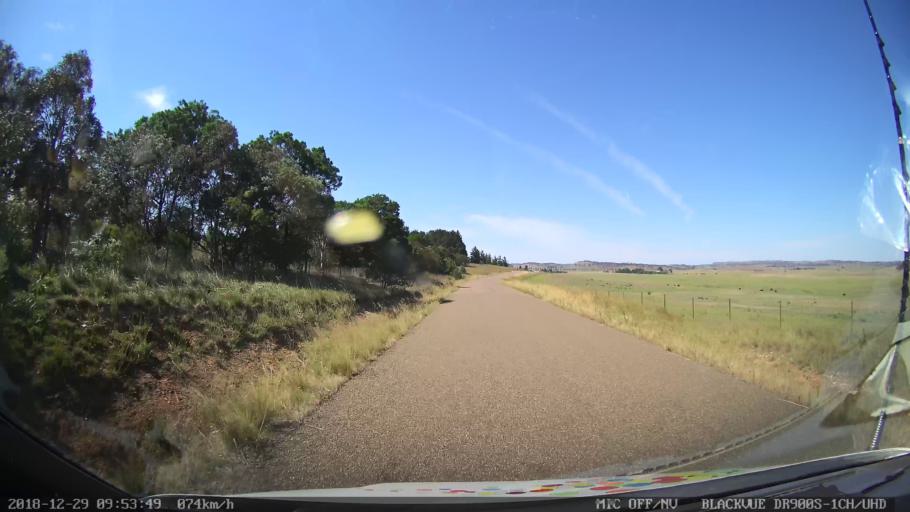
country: AU
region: New South Wales
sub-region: Goulburn Mulwaree
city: Goulburn
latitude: -34.7561
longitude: 149.4686
